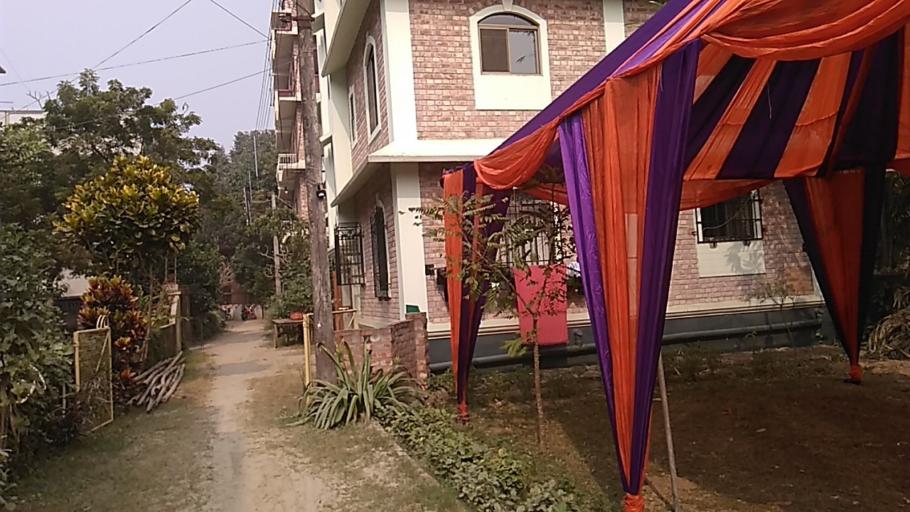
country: IN
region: West Bengal
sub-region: Nadia
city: Navadwip
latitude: 23.4156
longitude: 88.3845
